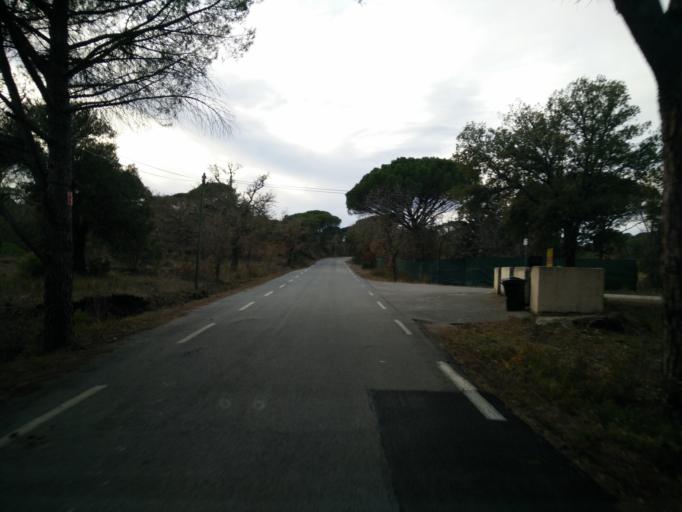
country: FR
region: Provence-Alpes-Cote d'Azur
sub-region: Departement du Var
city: Vidauban
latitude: 43.3935
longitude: 6.4742
